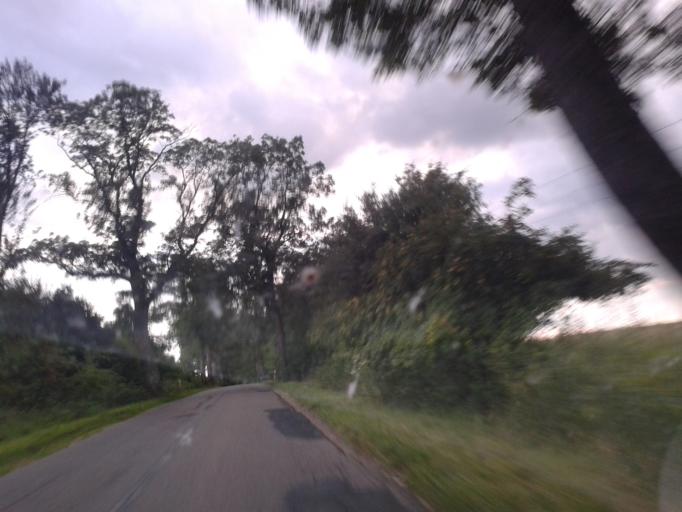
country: PL
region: West Pomeranian Voivodeship
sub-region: Powiat koszalinski
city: Bobolice
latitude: 53.8999
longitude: 16.5313
